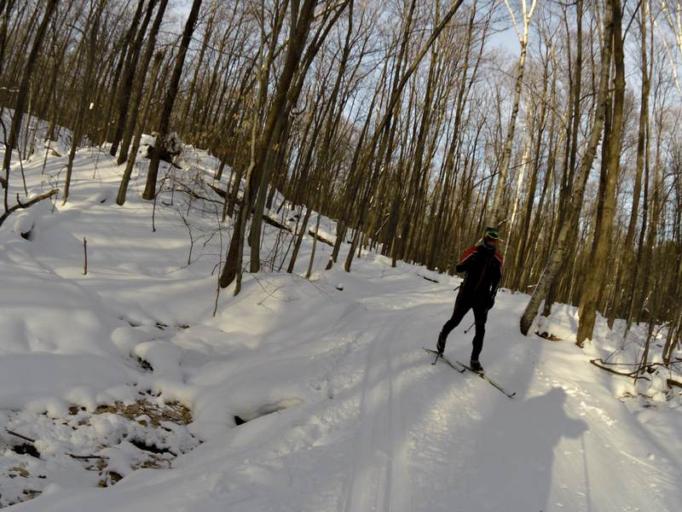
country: CA
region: Quebec
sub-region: Outaouais
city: Gatineau
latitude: 45.4743
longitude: -75.8098
